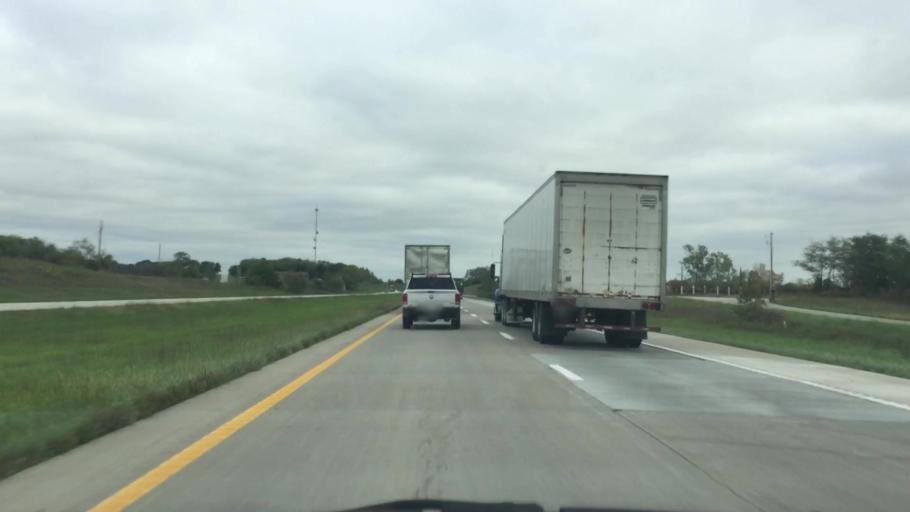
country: US
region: Missouri
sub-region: Clinton County
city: Lathrop
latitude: 39.5995
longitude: -94.2537
